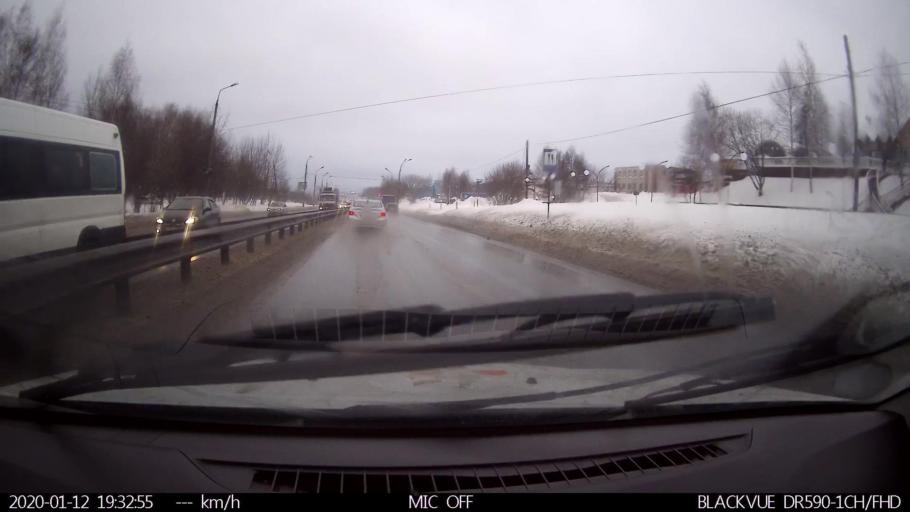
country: RU
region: Nizjnij Novgorod
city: Nizhniy Novgorod
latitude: 56.2402
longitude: 43.9990
